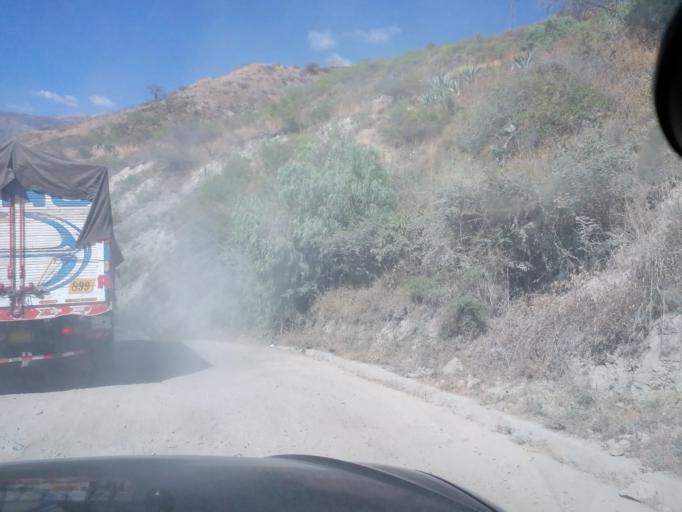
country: PE
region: Apurimac
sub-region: Provincia de Abancay
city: Curahuasi
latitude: -13.5441
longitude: -72.6774
